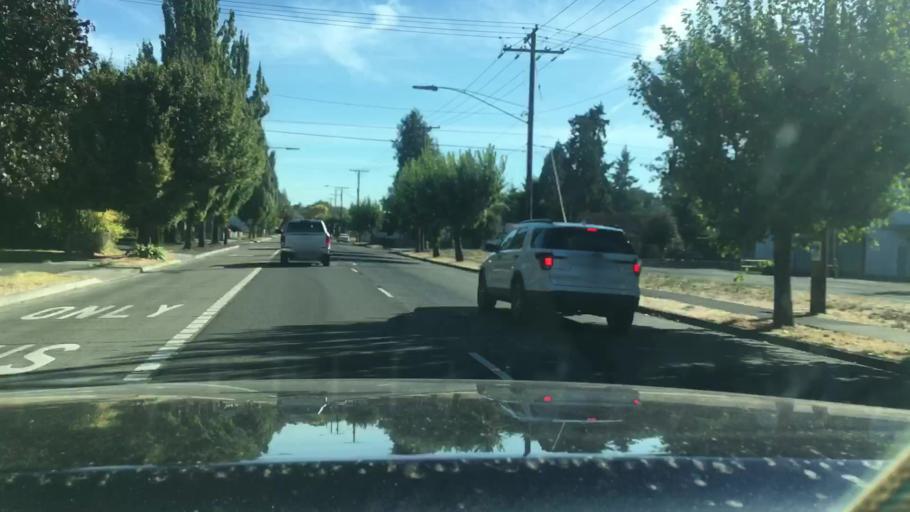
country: US
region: Oregon
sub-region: Lane County
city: Springfield
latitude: 44.0505
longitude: -123.0233
